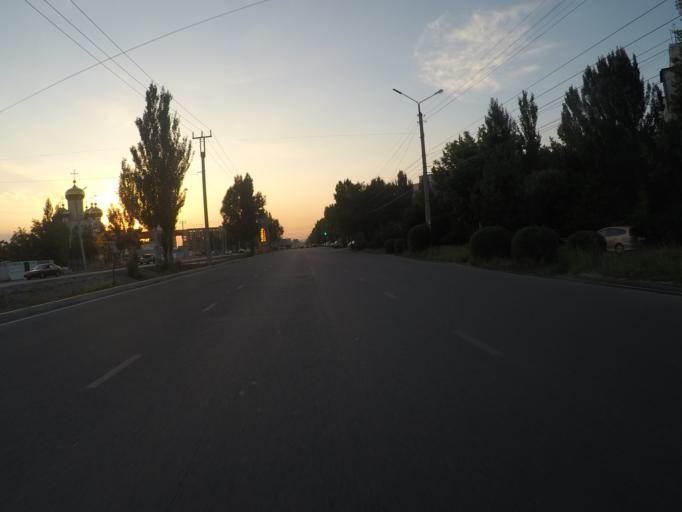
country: KG
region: Chuy
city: Bishkek
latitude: 42.8124
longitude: 74.6325
